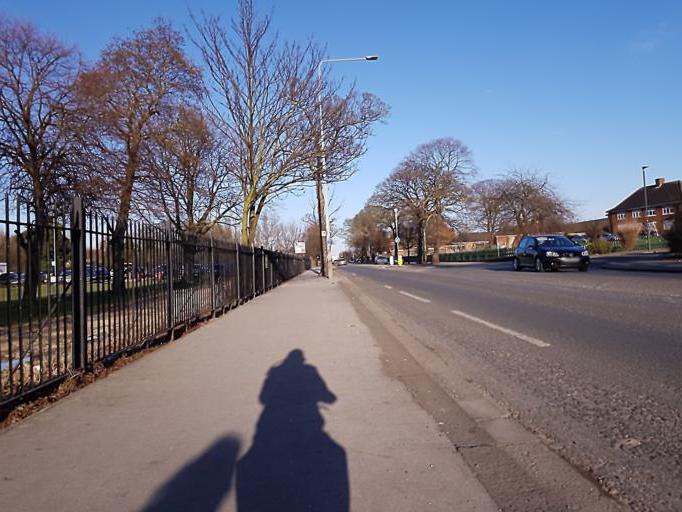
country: GB
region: England
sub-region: North East Lincolnshire
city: Cleethorpes
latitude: 53.5542
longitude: -0.0541
